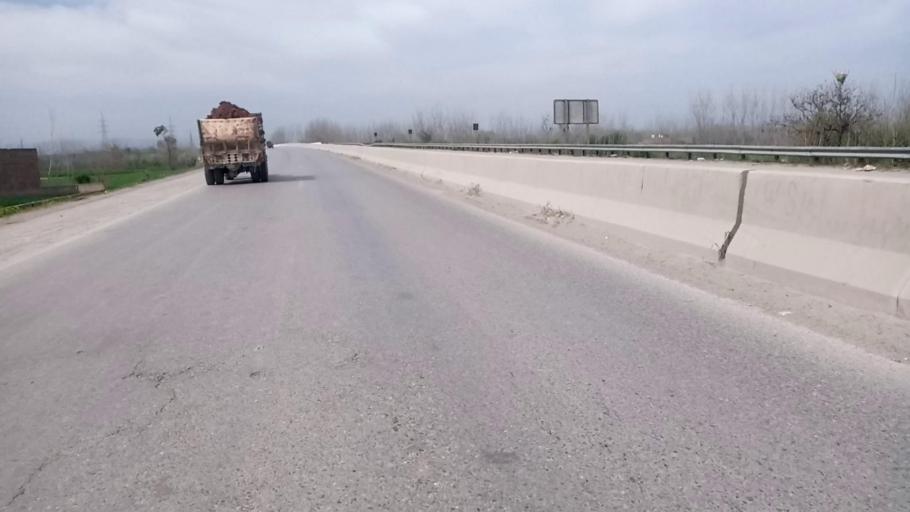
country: PK
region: Khyber Pakhtunkhwa
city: Peshawar
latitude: 34.0586
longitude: 71.6089
